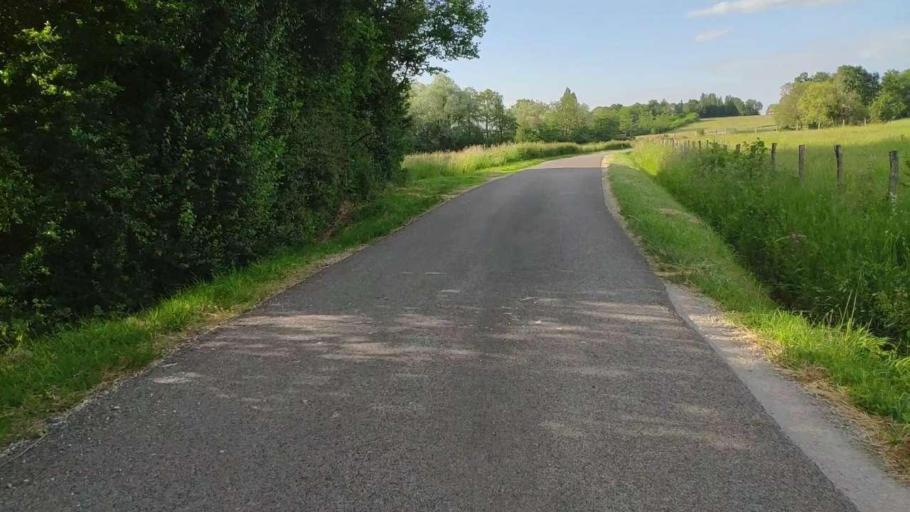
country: FR
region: Franche-Comte
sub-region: Departement du Jura
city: Bletterans
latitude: 46.7552
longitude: 5.4487
